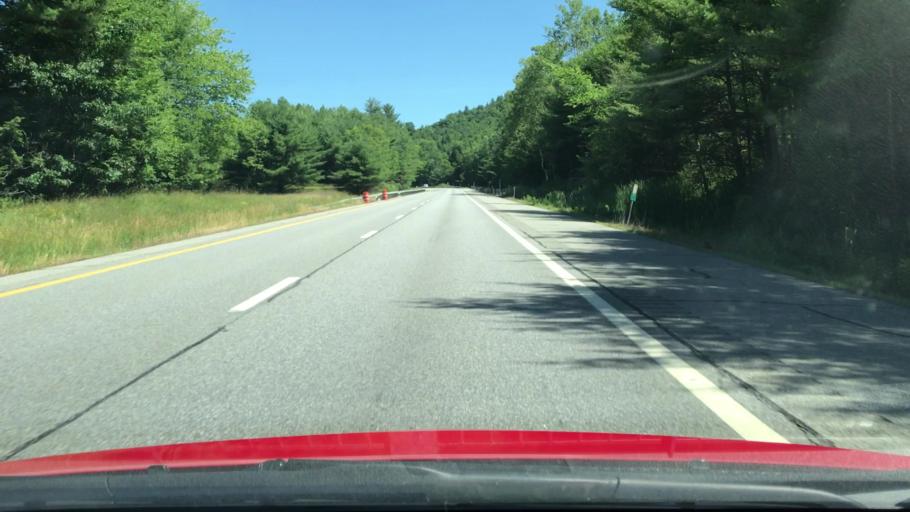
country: US
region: New York
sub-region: Warren County
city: Warrensburg
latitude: 43.5023
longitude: -73.7453
